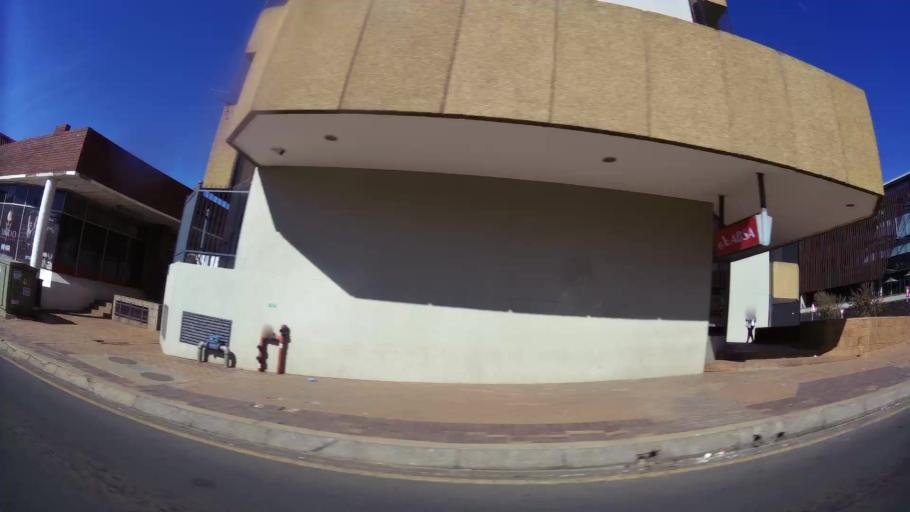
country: ZA
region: Gauteng
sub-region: City of Tshwane Metropolitan Municipality
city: Centurion
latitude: -25.8557
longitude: 28.1841
